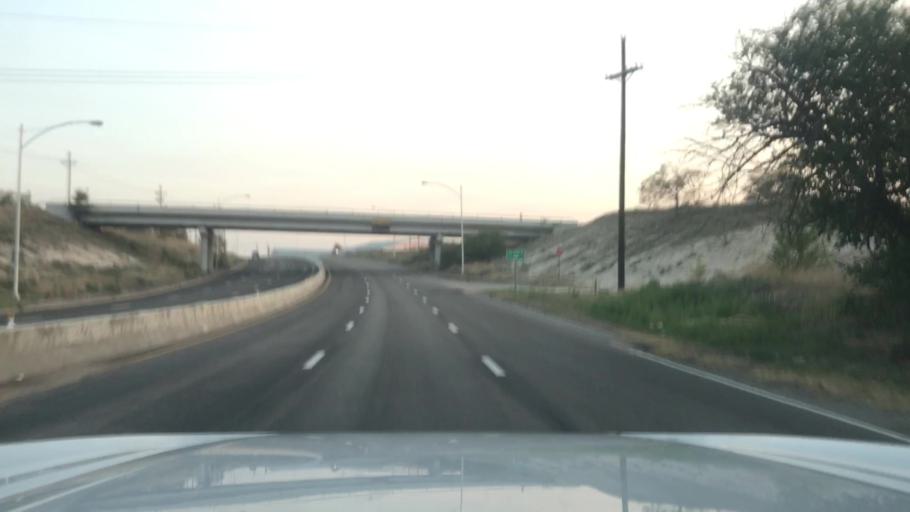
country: US
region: Texas
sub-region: Lubbock County
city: Lubbock
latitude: 33.6034
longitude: -101.8530
